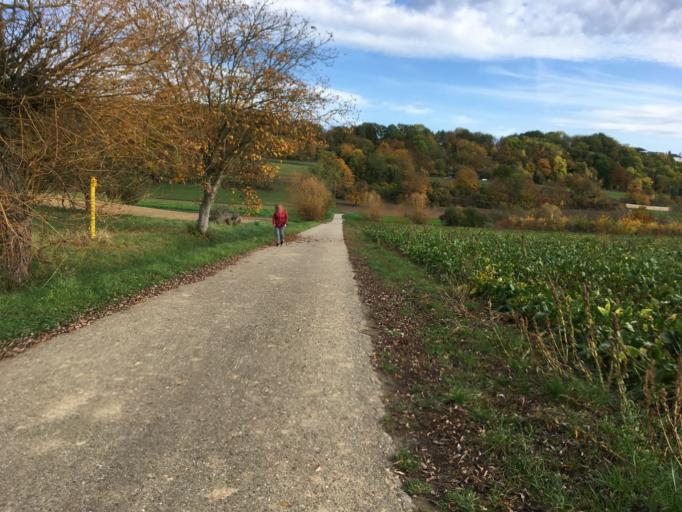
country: DE
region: Baden-Wuerttemberg
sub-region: Karlsruhe Region
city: Sinsheim
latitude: 49.2621
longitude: 8.9023
